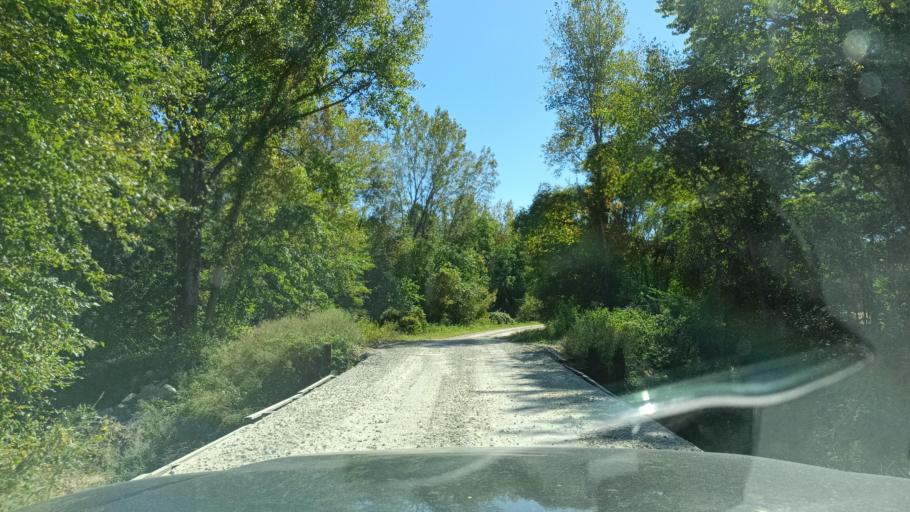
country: US
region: Missouri
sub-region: Macon County
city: La Plata
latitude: 39.9655
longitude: -92.6435
